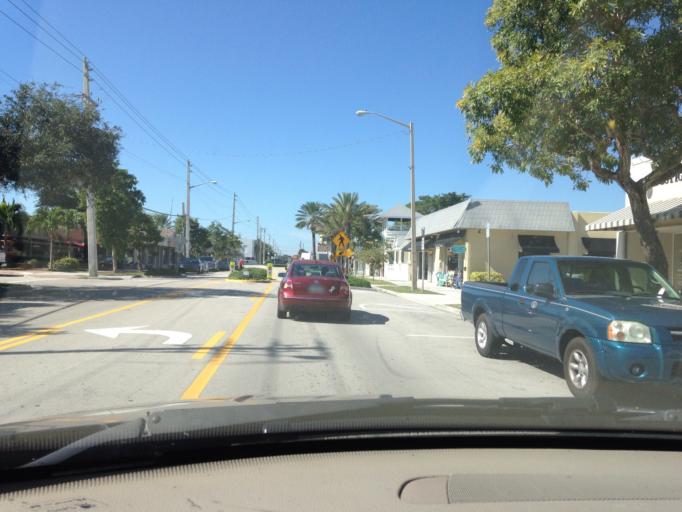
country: US
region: Florida
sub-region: Martin County
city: Stuart
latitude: 27.1975
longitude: -80.2513
